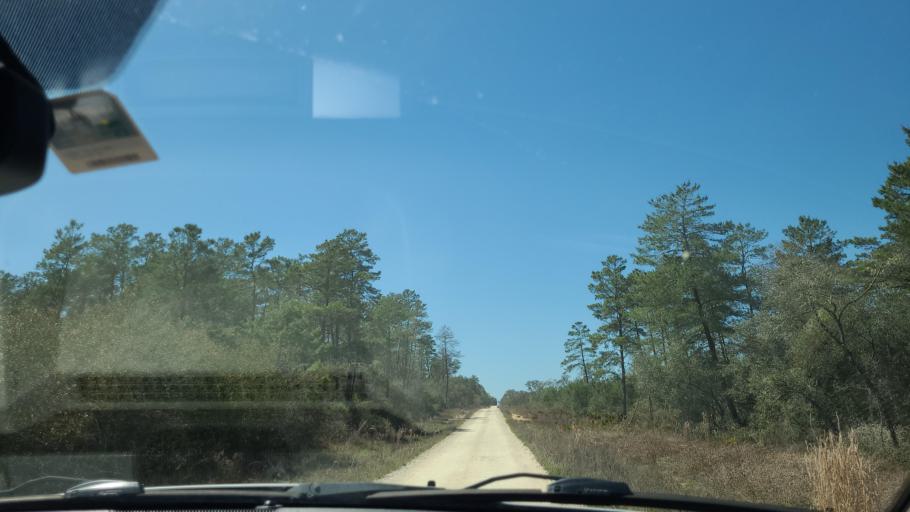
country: US
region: Florida
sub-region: Putnam County
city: Interlachen
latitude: 29.4283
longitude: -81.9038
